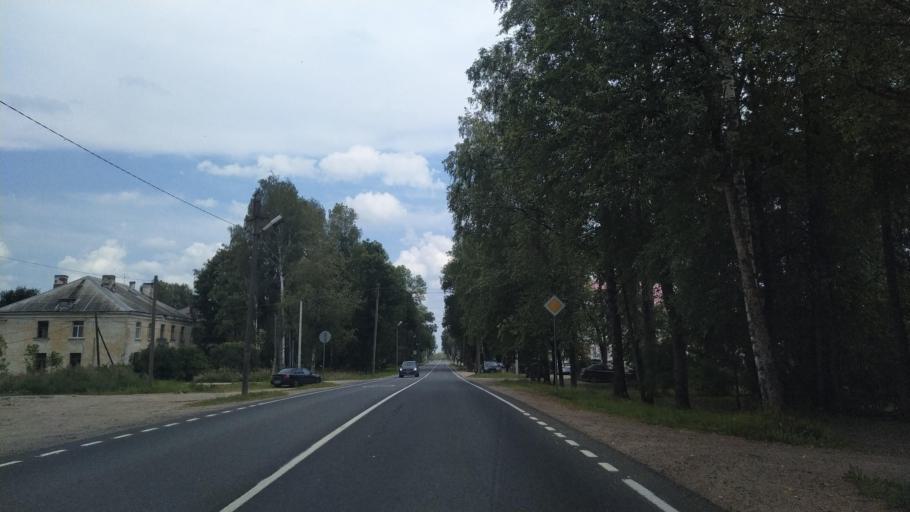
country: RU
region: Pskov
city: Pskov
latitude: 57.7619
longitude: 28.7566
